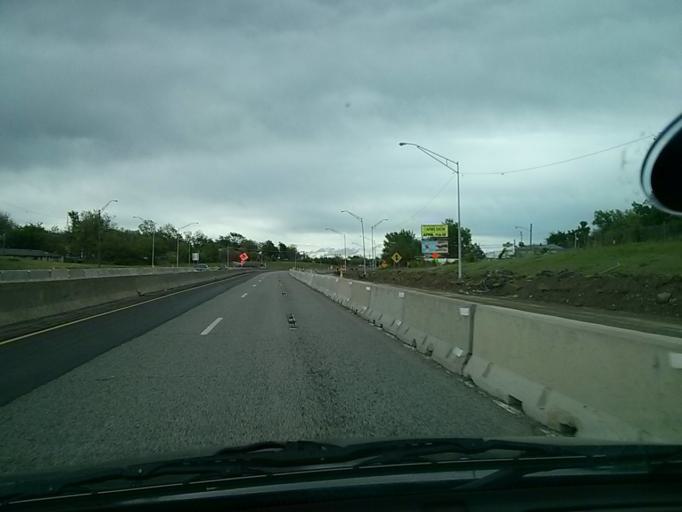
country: US
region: Oklahoma
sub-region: Tulsa County
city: Tulsa
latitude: 36.1597
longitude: -95.9649
